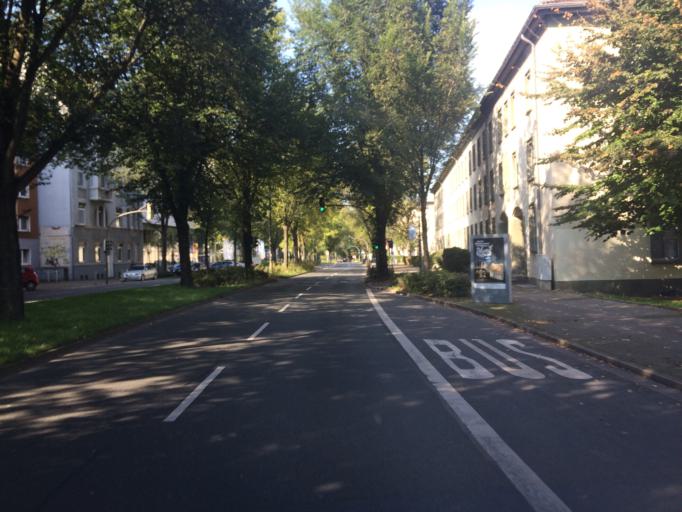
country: DE
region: North Rhine-Westphalia
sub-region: Regierungsbezirk Arnsberg
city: Dortmund
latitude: 51.5013
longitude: 7.4819
